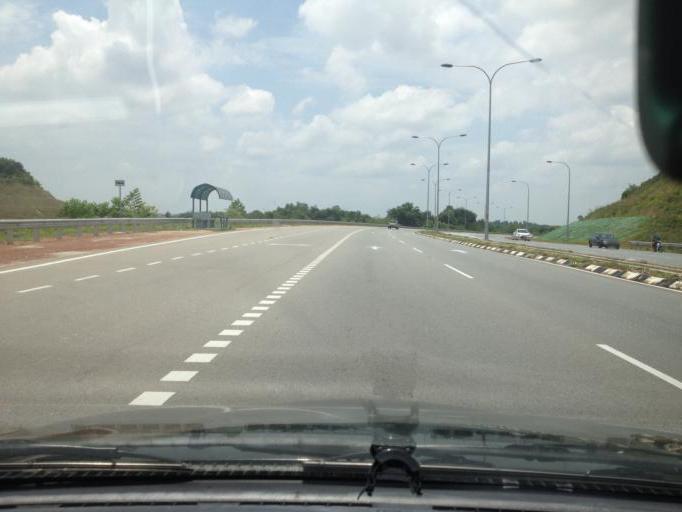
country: MY
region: Kedah
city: Sungai Petani
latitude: 5.6114
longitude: 100.5677
